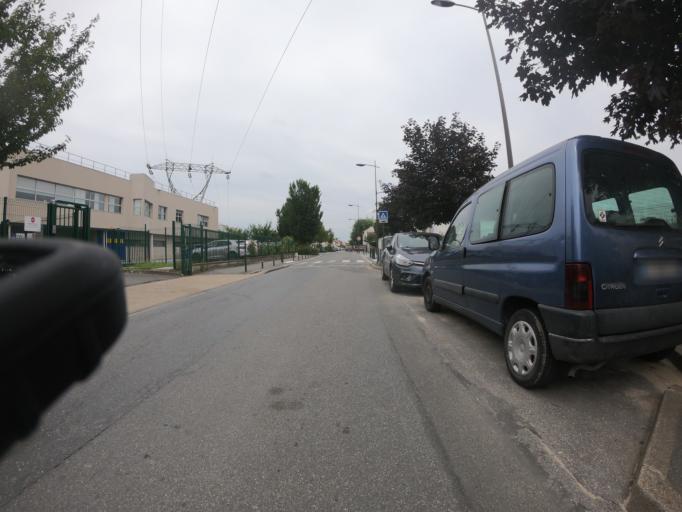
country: FR
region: Ile-de-France
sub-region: Departement du Val-de-Marne
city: Thiais
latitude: 48.7597
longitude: 2.3872
